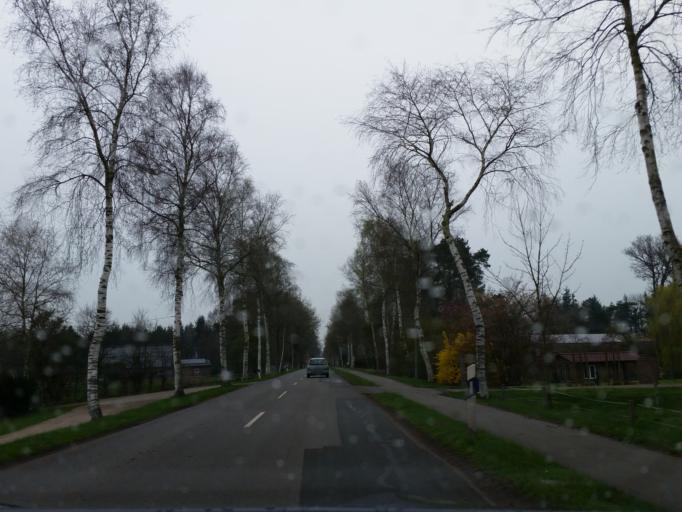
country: DE
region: Lower Saxony
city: Bei der Hohne
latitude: 53.5347
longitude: 9.1253
